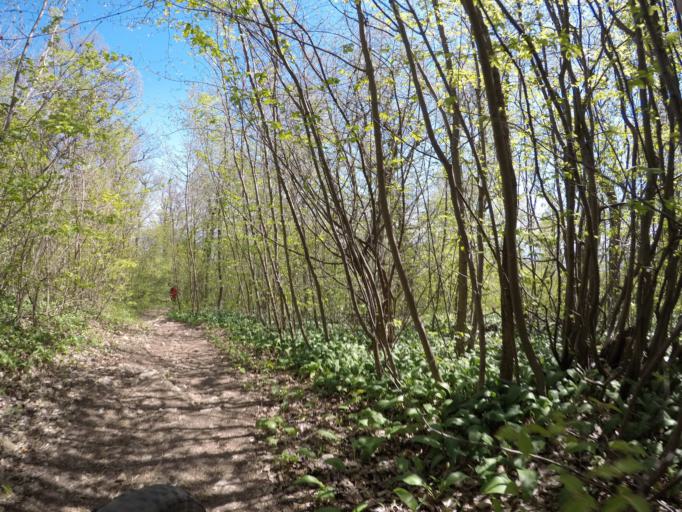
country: AT
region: Lower Austria
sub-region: Politischer Bezirk Modling
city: Gumpoldskirchen
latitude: 48.0506
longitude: 16.2543
